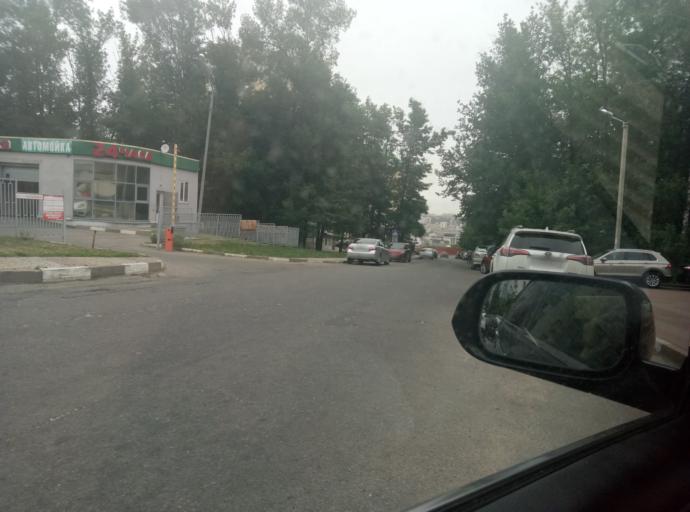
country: RU
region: Belgorod
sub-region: Belgorodskiy Rayon
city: Belgorod
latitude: 50.5799
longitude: 36.5868
